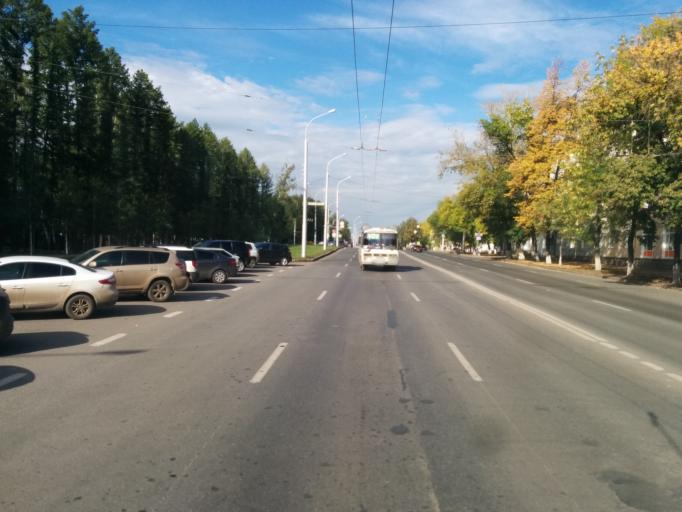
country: RU
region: Bashkortostan
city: Ufa
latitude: 54.8207
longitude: 56.0575
